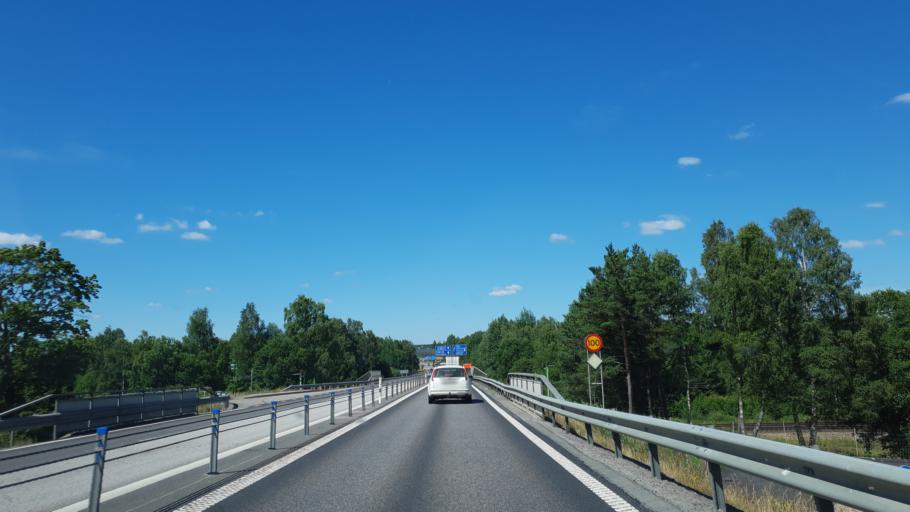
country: SE
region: Kronoberg
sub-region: Alvesta Kommun
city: Alvesta
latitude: 56.9217
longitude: 14.5686
